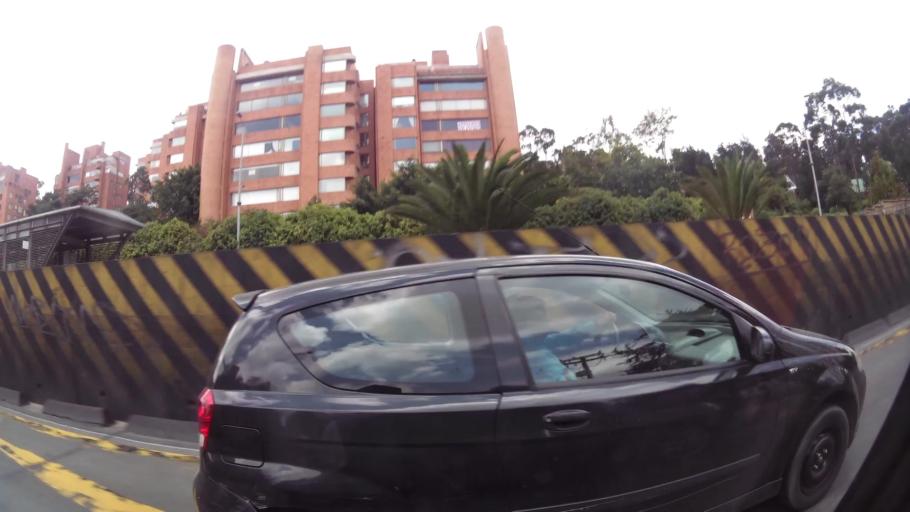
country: CO
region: Bogota D.C.
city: Barrio San Luis
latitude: 4.7281
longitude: -74.0746
